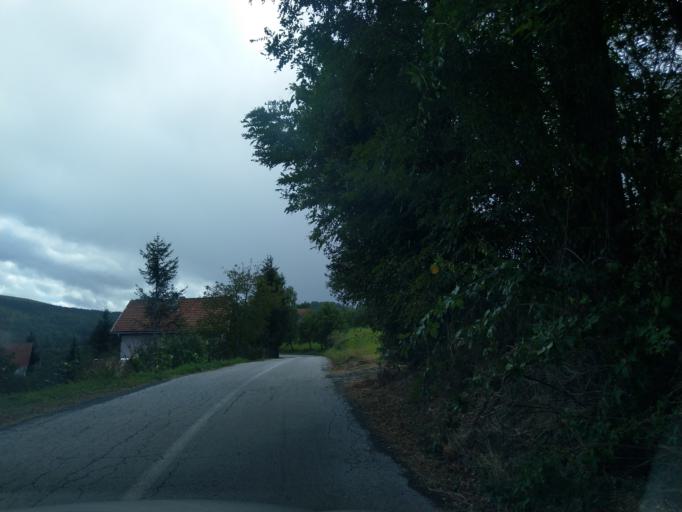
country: RS
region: Central Serbia
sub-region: Zlatiborski Okrug
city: Cajetina
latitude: 43.6886
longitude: 19.8478
